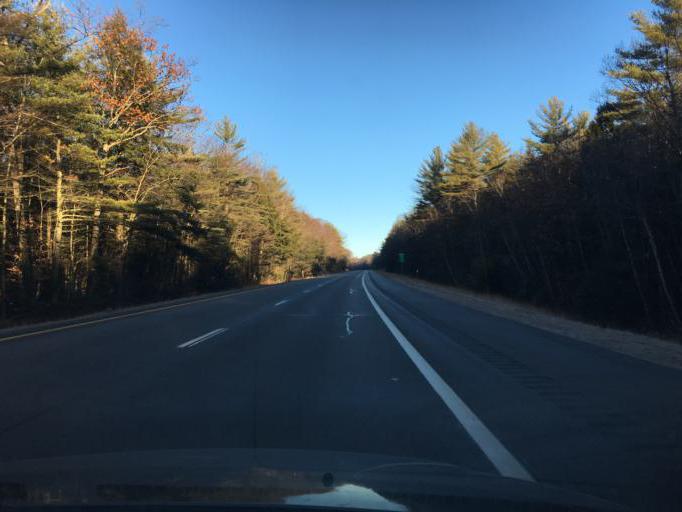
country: US
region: New Hampshire
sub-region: Belknap County
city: Sanbornton
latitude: 43.4851
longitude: -71.5925
